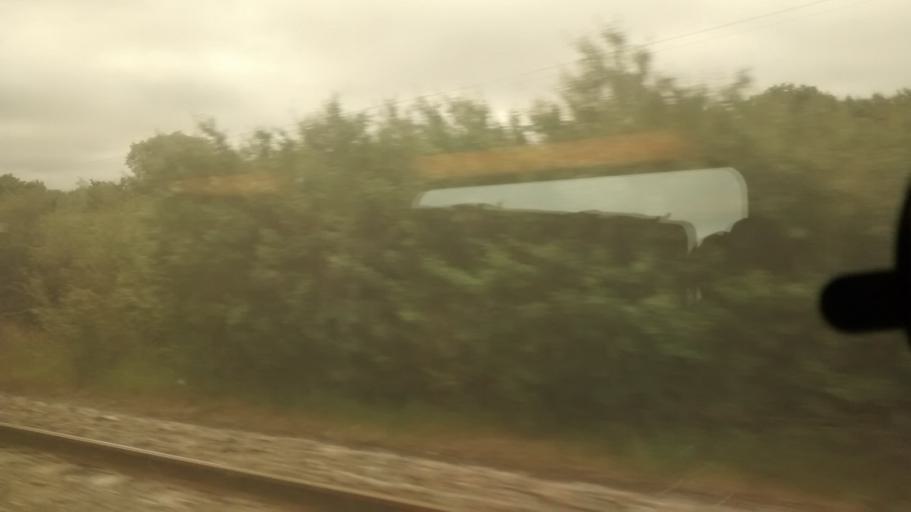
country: FR
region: Centre
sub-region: Departement d'Eure-et-Loir
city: Bonneval
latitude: 48.2175
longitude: 1.4338
